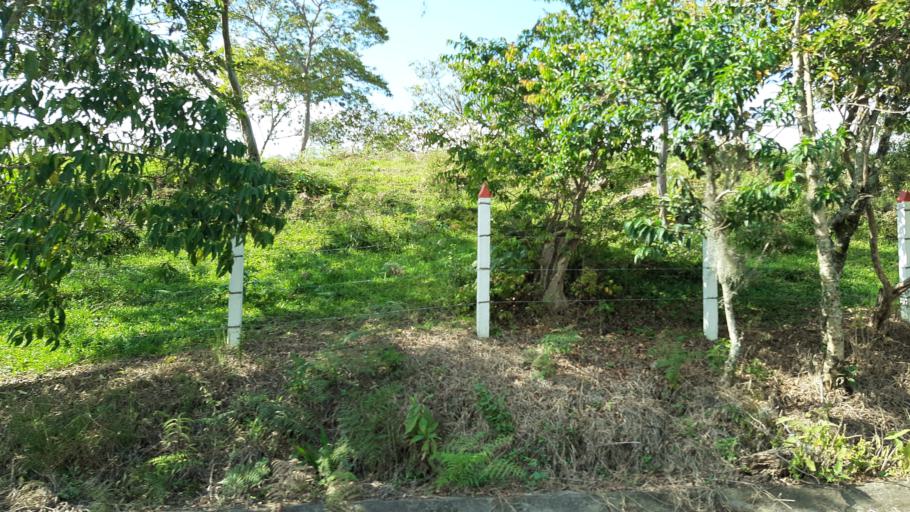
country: CO
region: Boyaca
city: Moniquira
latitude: 5.8135
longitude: -73.5998
